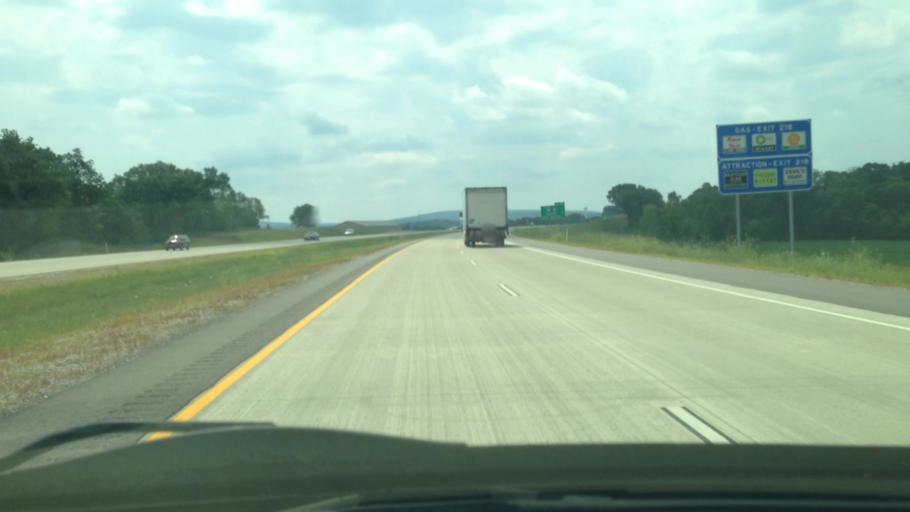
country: US
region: Wisconsin
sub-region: Sauk County
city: West Baraboo
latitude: 43.4823
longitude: -89.7751
